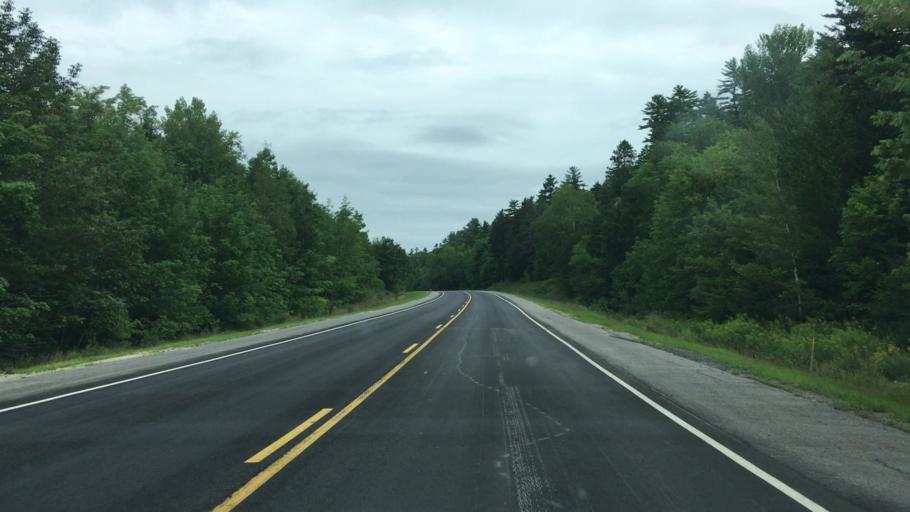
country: US
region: Maine
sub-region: Washington County
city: Cherryfield
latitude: 44.8968
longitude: -67.8557
